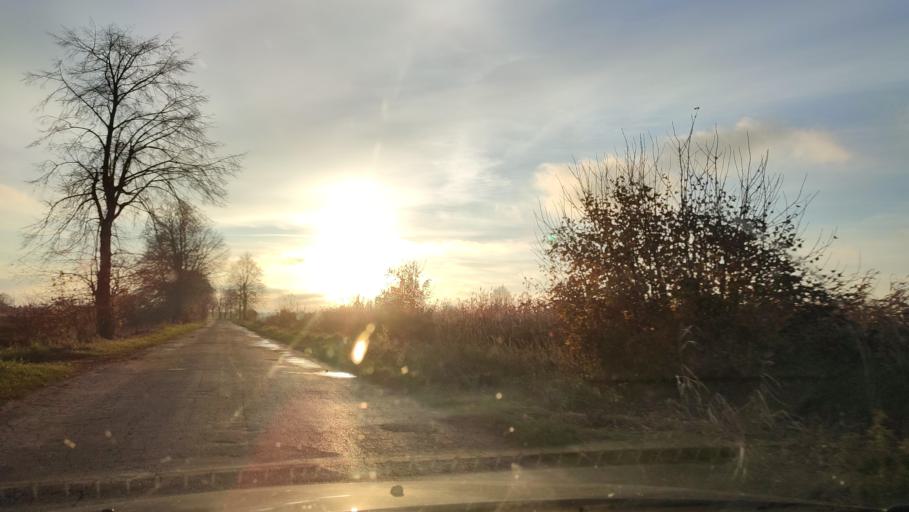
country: PL
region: Masovian Voivodeship
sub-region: Powiat mlawski
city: Wieczfnia Koscielna
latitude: 53.2504
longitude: 20.5861
